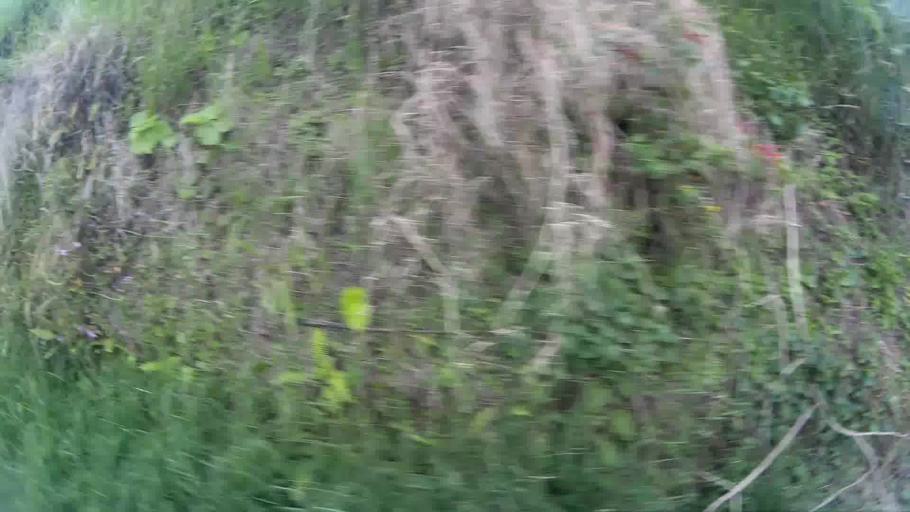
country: CO
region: Risaralda
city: Pereira
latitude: 4.7669
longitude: -75.7190
